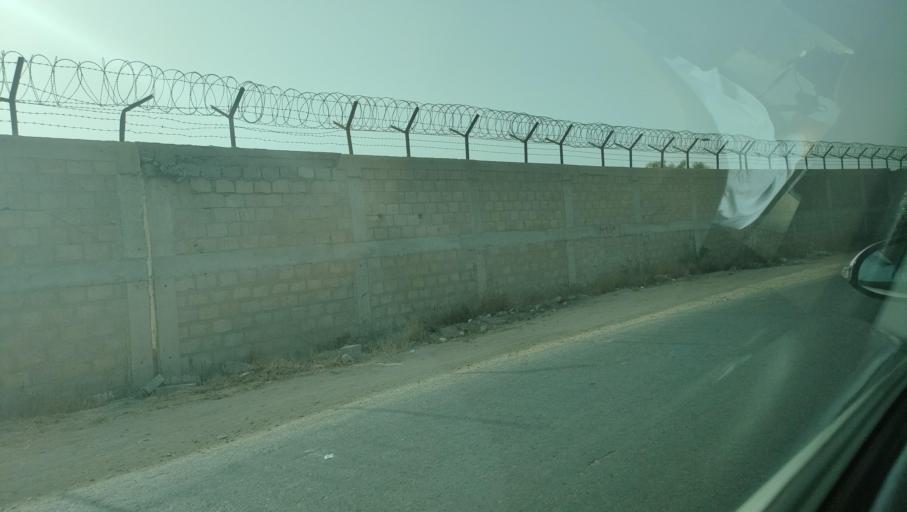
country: PK
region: Sindh
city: Malir Cantonment
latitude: 24.9148
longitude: 67.1883
